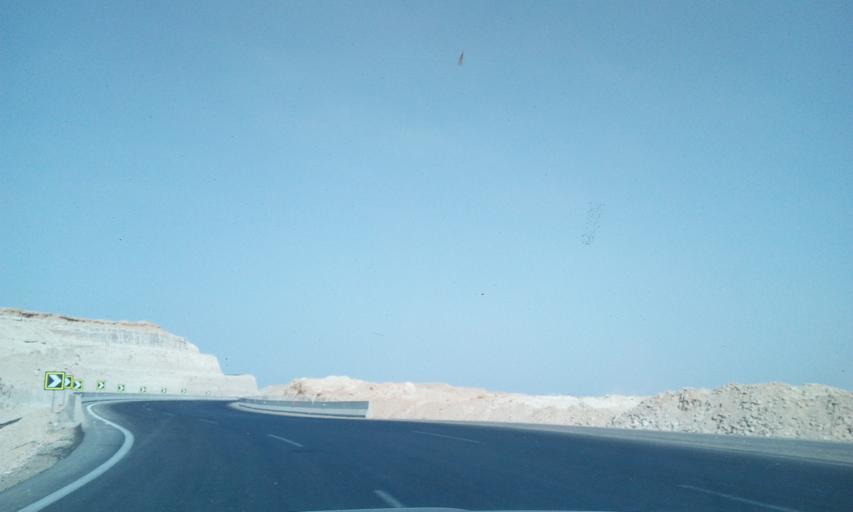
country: EG
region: As Suways
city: Ain Sukhna
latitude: 29.6649
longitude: 32.2356
